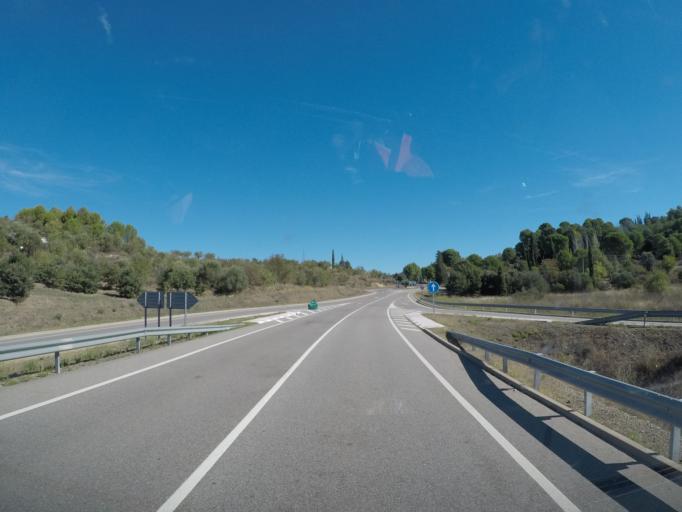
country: ES
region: Catalonia
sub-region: Provincia de Tarragona
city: Falset
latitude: 41.1408
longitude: 0.8097
